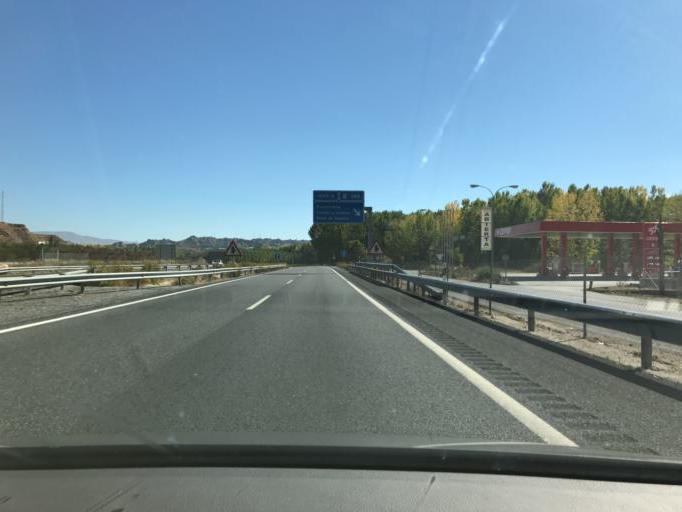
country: ES
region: Andalusia
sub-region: Provincia de Granada
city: Purullena
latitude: 37.3299
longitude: -3.2181
